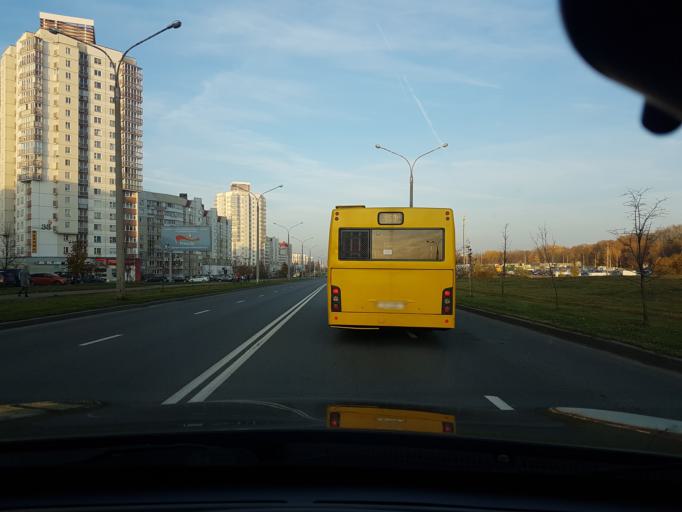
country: BY
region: Minsk
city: Shchomyslitsa
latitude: 53.8443
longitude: 27.4841
